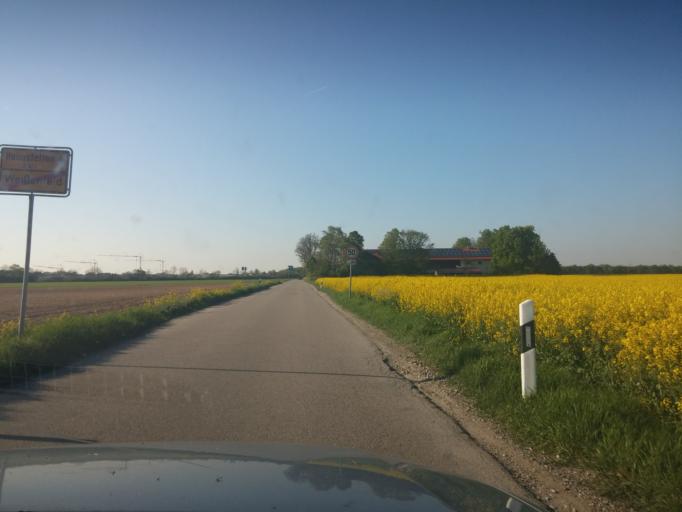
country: DE
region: Bavaria
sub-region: Upper Bavaria
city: Vaterstetten
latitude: 48.1373
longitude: 11.7633
